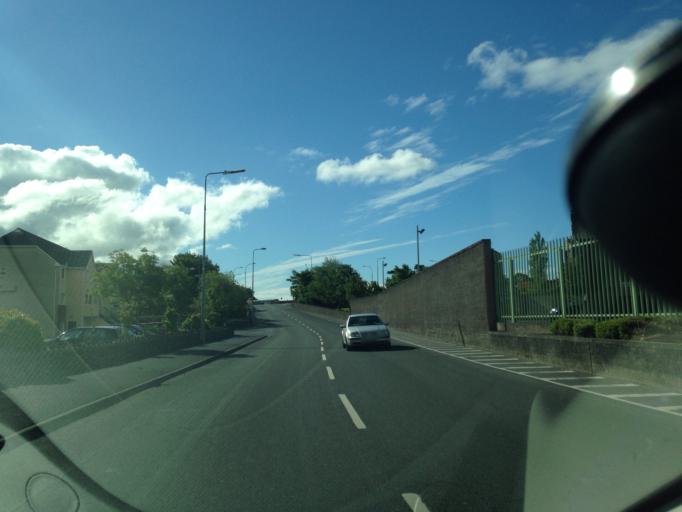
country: IE
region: Connaught
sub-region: County Galway
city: Gaillimh
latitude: 53.2836
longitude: -9.0398
